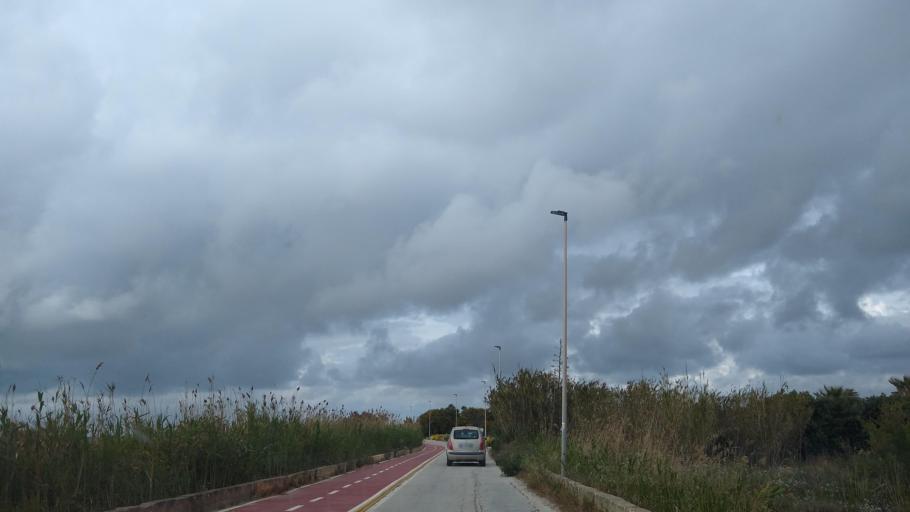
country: IT
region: Sicily
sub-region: Trapani
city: Marsala
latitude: 37.8593
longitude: 12.4850
